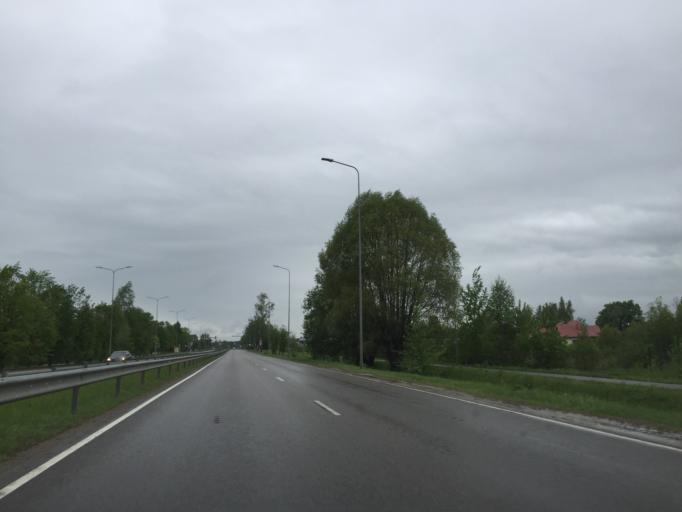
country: LV
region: Ogre
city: Ogre
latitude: 56.8008
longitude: 24.6175
